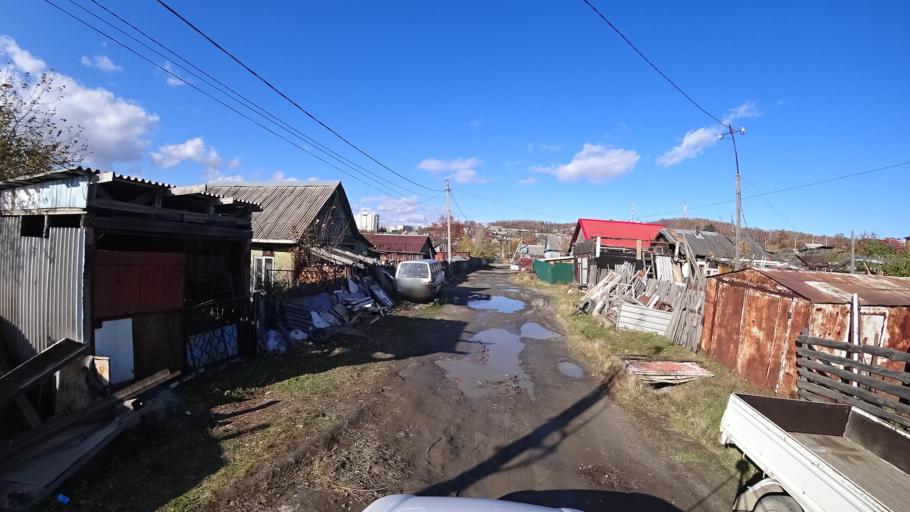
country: RU
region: Khabarovsk Krai
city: Amursk
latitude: 50.2344
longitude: 136.9212
